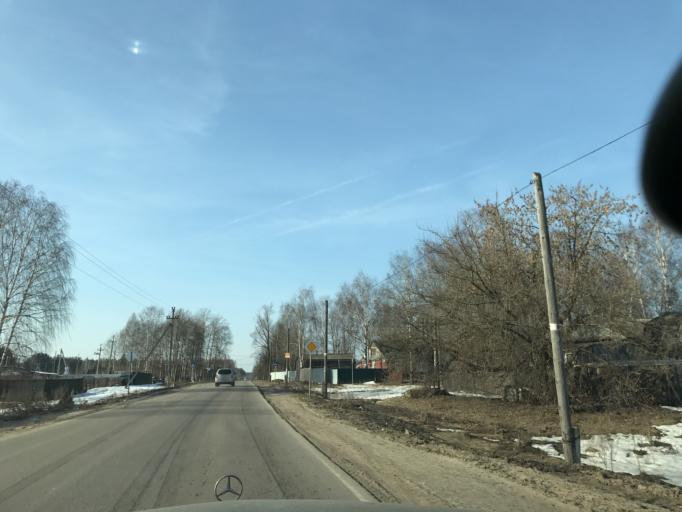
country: RU
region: Nizjnij Novgorod
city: Taremskoye
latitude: 55.9979
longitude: 43.0041
